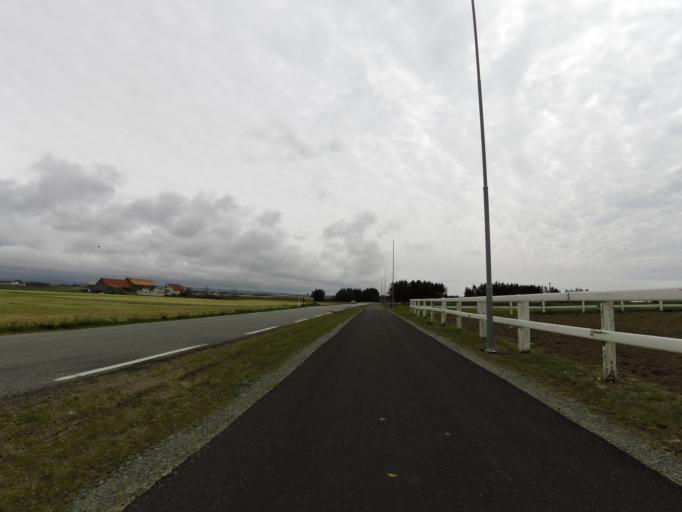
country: NO
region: Rogaland
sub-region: Ha
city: Naerbo
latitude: 58.6925
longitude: 5.5563
